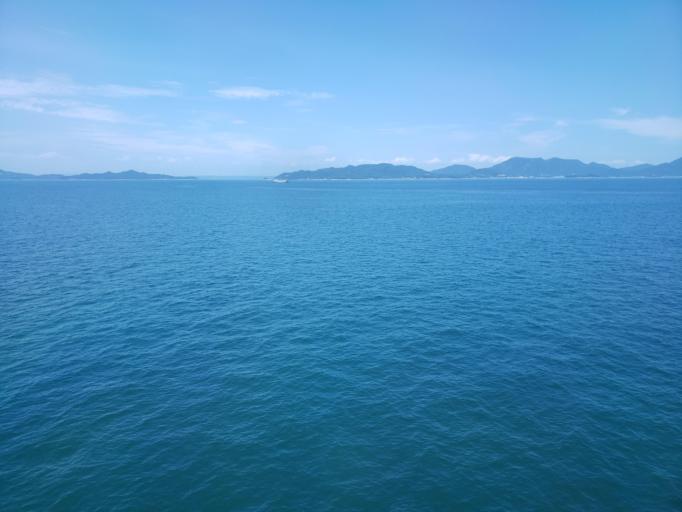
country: JP
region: Kagawa
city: Tonosho
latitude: 34.4058
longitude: 134.1545
